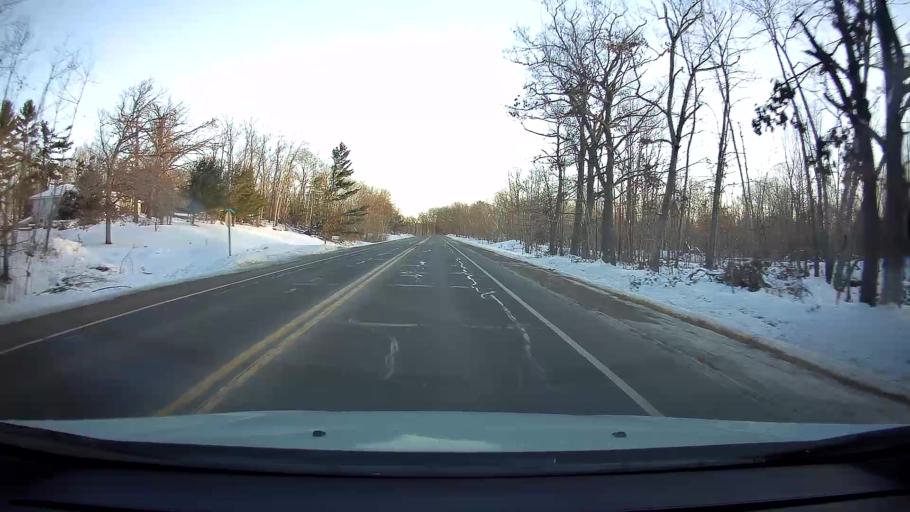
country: US
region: Wisconsin
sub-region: Barron County
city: Turtle Lake
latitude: 45.4122
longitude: -92.1349
